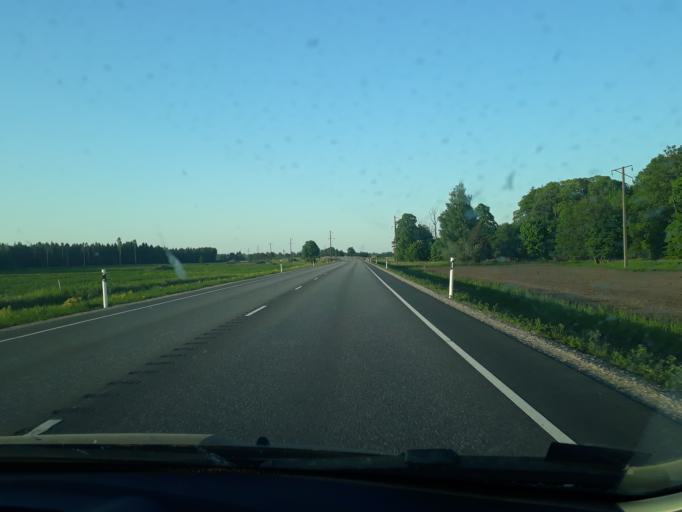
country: EE
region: Paernumaa
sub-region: Tootsi vald
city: Tootsi
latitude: 58.5734
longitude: 24.8802
